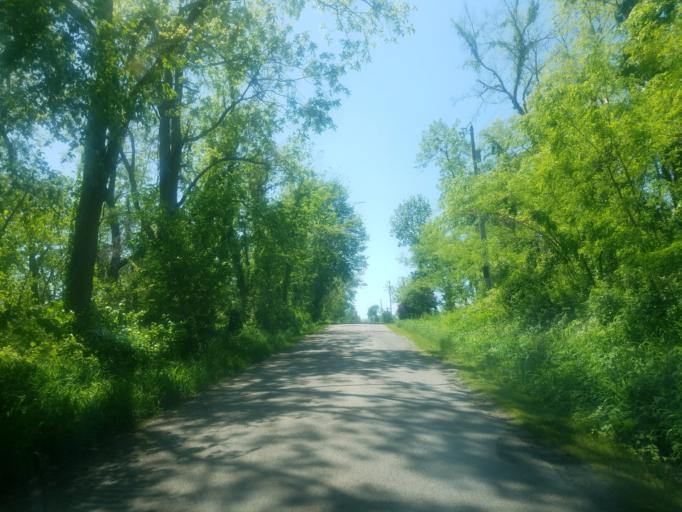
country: US
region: Ohio
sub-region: Huron County
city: Wakeman
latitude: 41.1918
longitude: -82.3702
